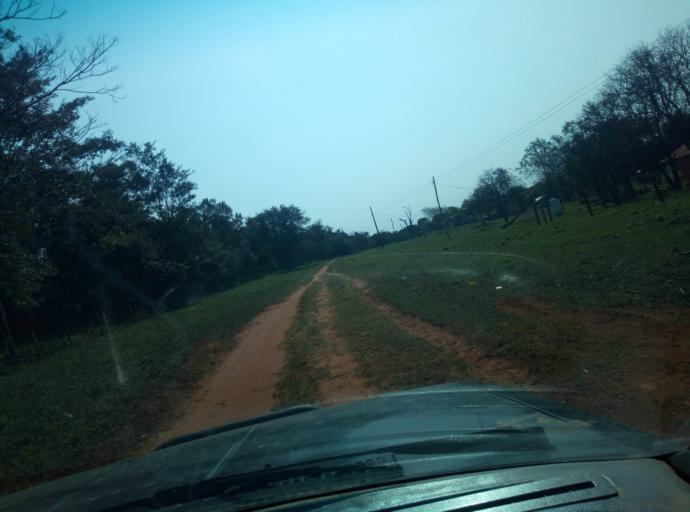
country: PY
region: Caaguazu
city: Carayao
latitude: -25.3055
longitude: -56.3247
